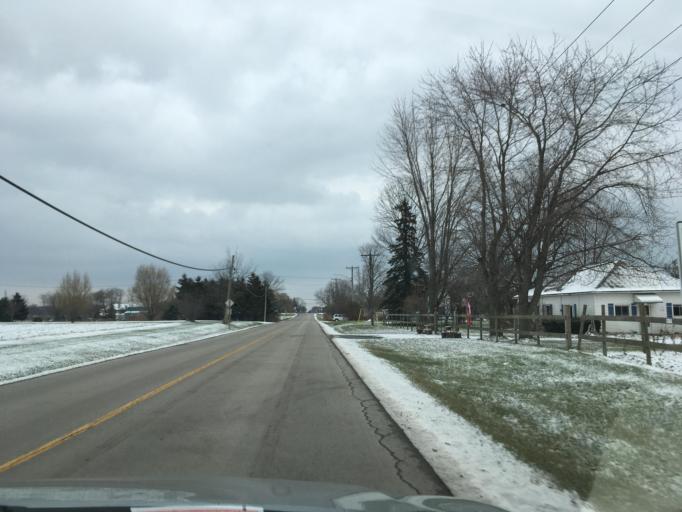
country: CA
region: Ontario
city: Norfolk County
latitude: 42.8115
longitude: -80.0668
